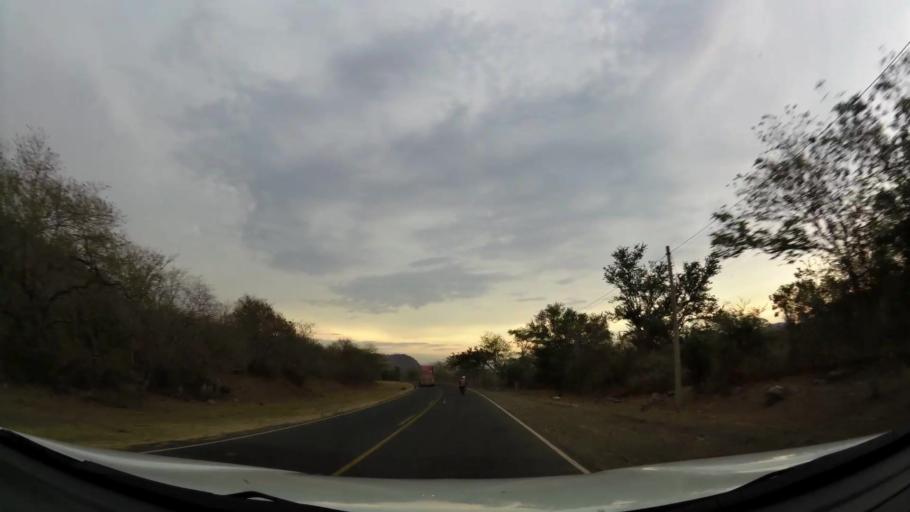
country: NI
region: Leon
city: La Jicaral
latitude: 12.7080
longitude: -86.3955
